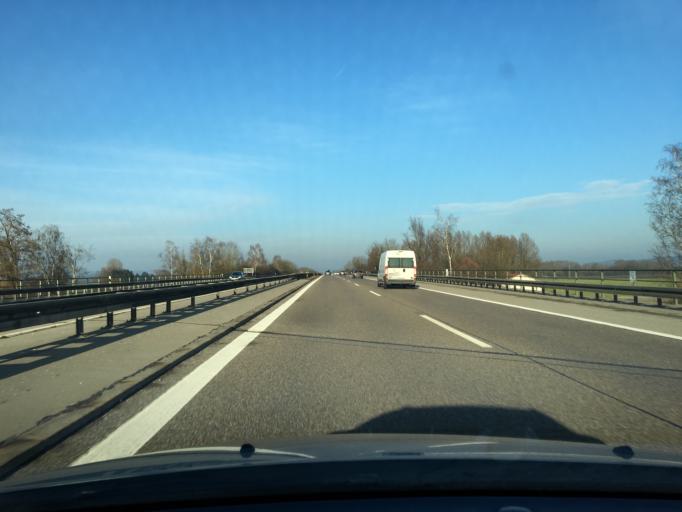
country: DE
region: Bavaria
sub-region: Upper Bavaria
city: Langenpreising
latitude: 48.4613
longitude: 11.9758
